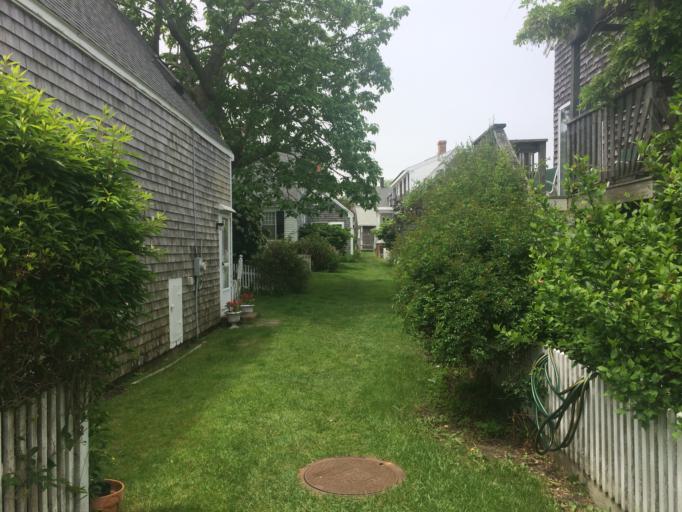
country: US
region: Massachusetts
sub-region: Barnstable County
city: Provincetown
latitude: 42.0431
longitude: -70.1930
